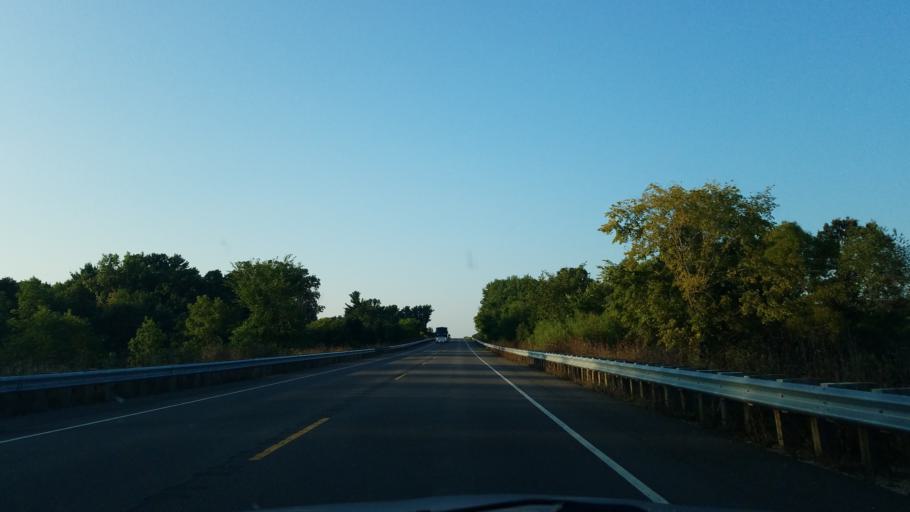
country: US
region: Wisconsin
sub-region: Polk County
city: Clear Lake
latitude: 45.2005
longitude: -92.2837
